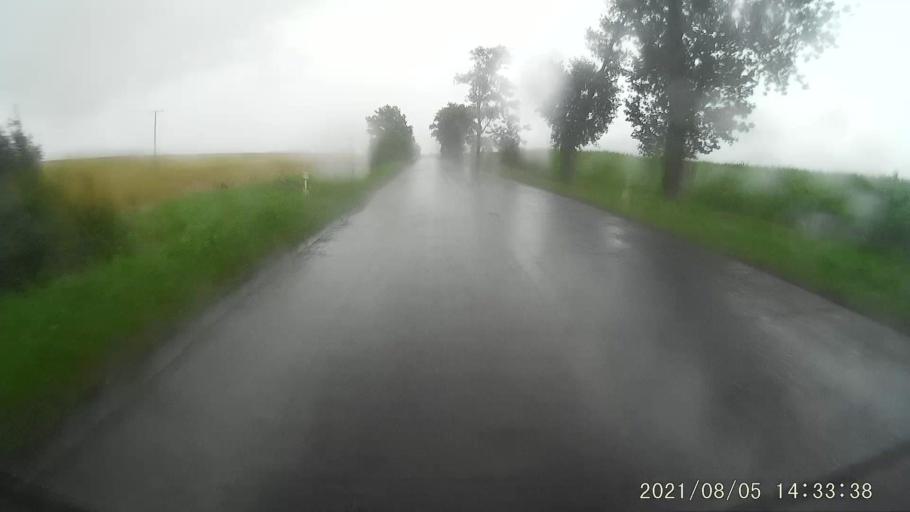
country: PL
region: Opole Voivodeship
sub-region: Powiat nyski
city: Korfantow
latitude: 50.4686
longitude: 17.5338
